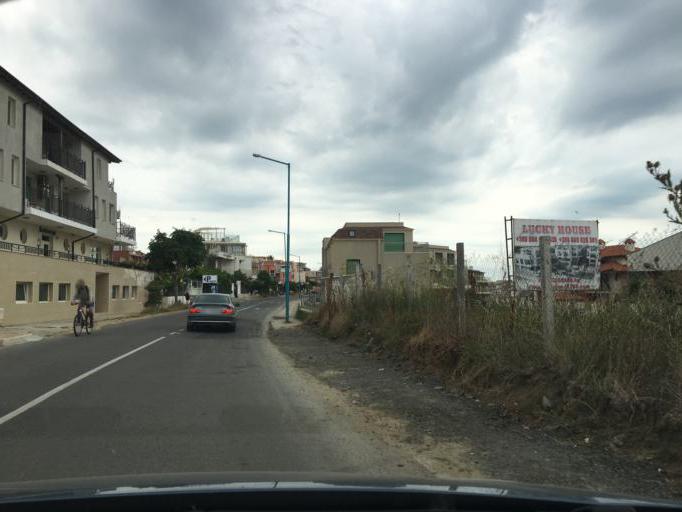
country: BG
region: Burgas
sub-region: Obshtina Sozopol
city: Sozopol
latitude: 42.4082
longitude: 27.7047
